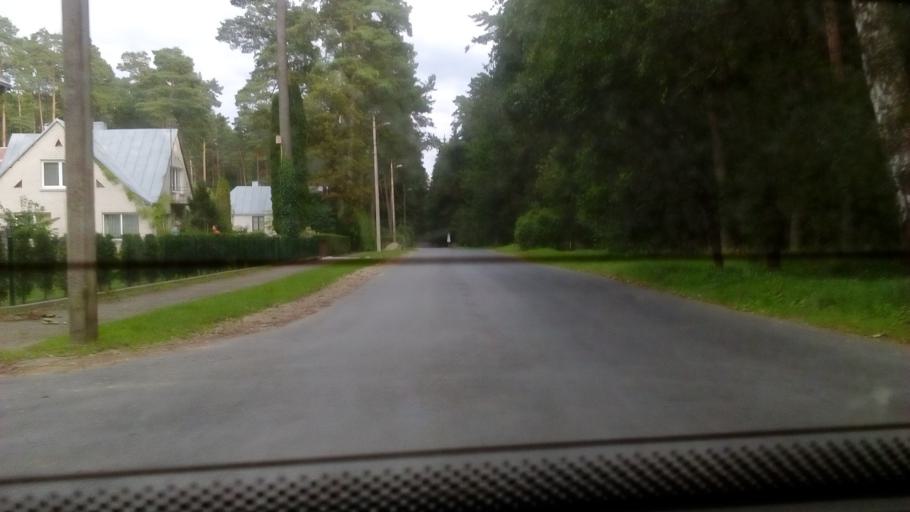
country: LT
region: Alytaus apskritis
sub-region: Alytus
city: Alytus
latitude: 54.3931
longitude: 24.0654
